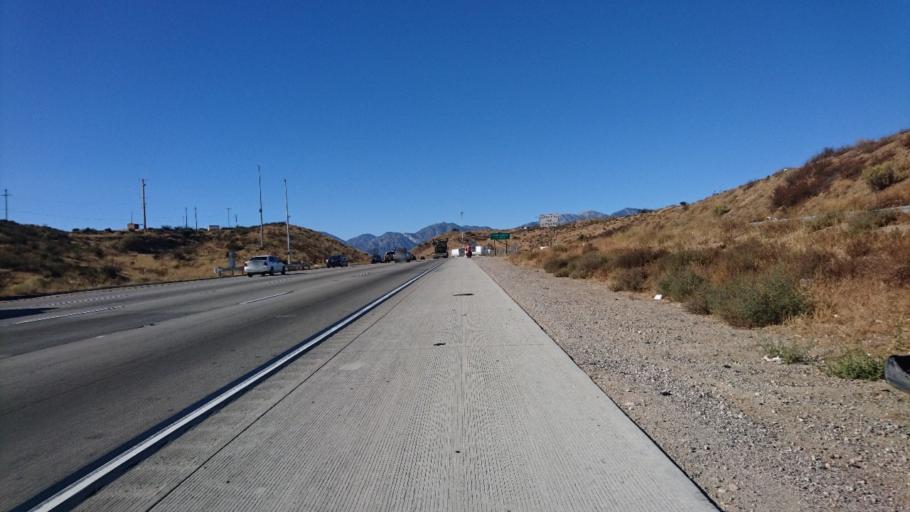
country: US
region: California
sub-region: San Bernardino County
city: Oak Hills
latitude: 34.3511
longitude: -117.4443
